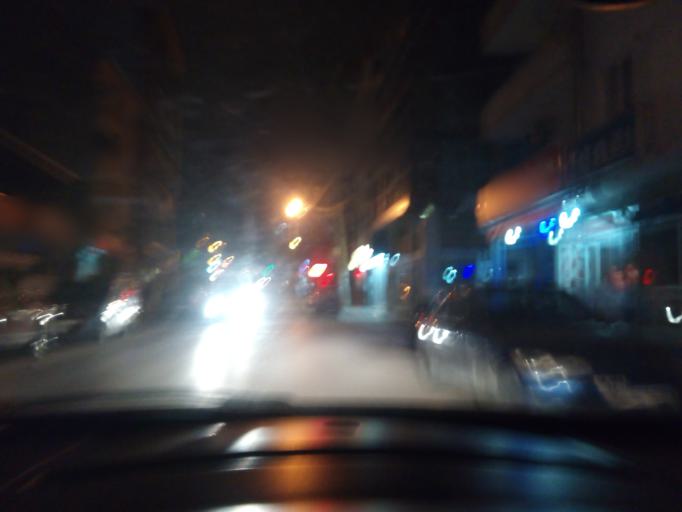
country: TR
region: Bursa
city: Niluefer
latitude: 40.2579
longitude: 28.9630
